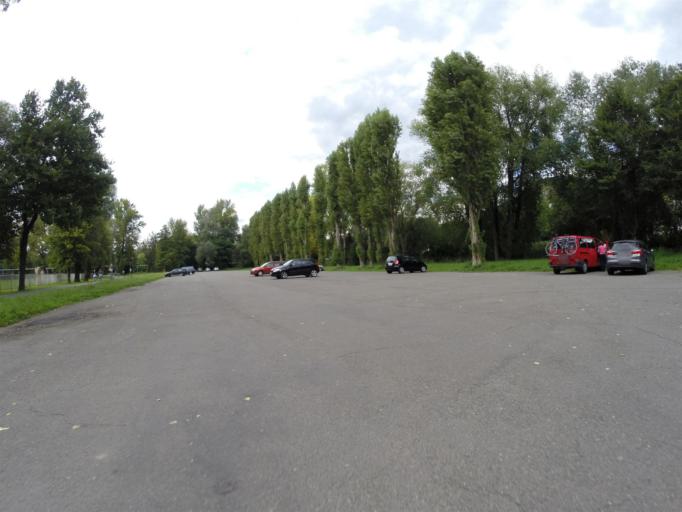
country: DE
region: Thuringia
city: Jena
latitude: 50.9158
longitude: 11.5869
